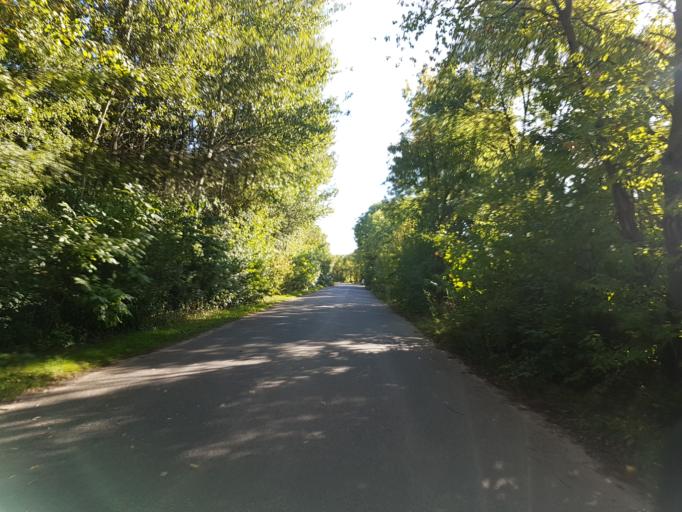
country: DE
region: North Rhine-Westphalia
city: Porta Westfalica
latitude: 52.2591
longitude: 8.9237
